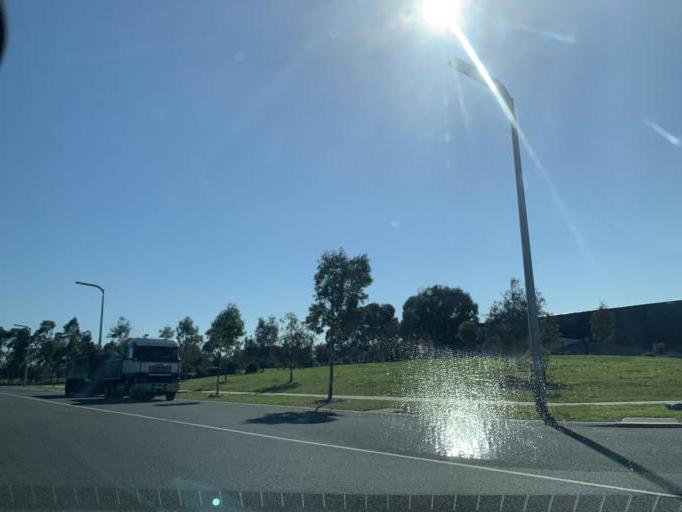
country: AU
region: Victoria
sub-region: Greater Dandenong
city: Dandenong
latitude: -38.0038
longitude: 145.1987
